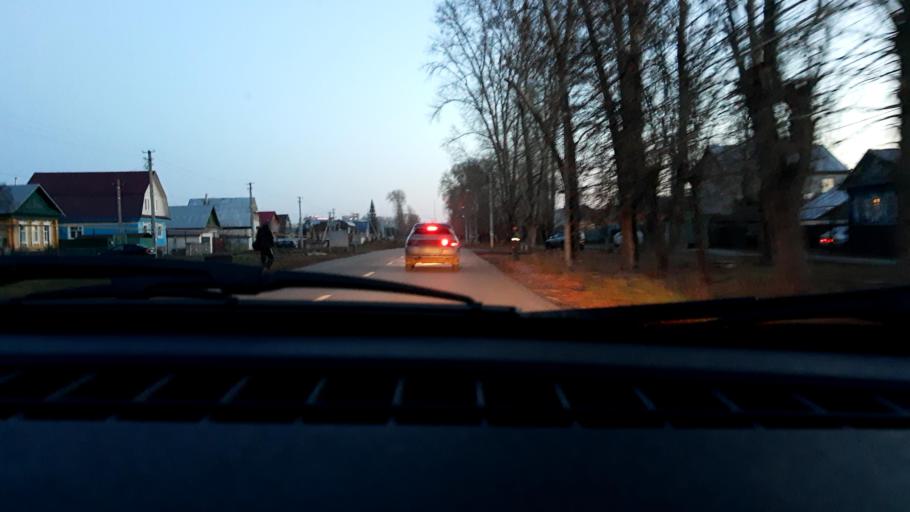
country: RU
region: Bashkortostan
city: Mikhaylovka
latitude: 54.7668
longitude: 55.8972
